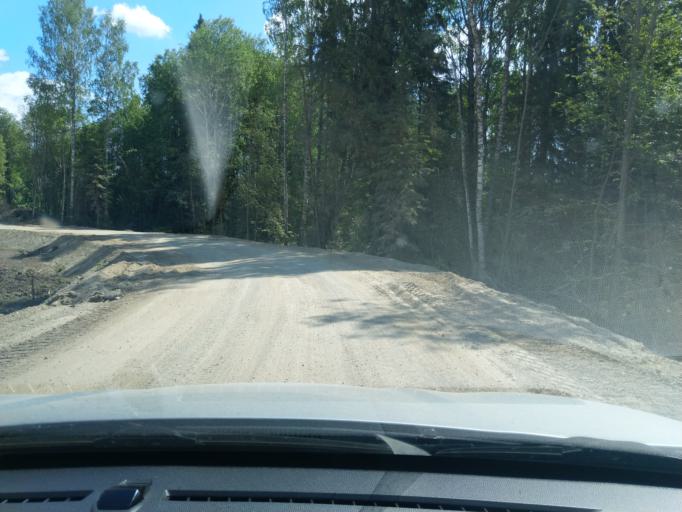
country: RU
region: Perm
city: Pozhva
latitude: 59.4195
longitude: 56.2484
